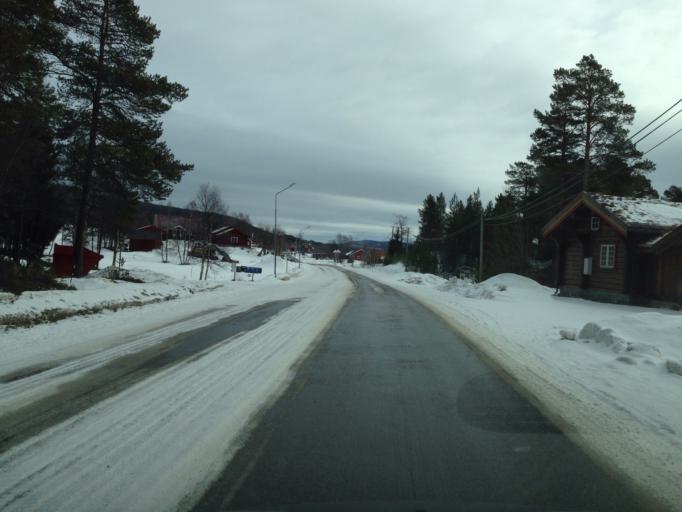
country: SE
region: Jaemtland
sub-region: Harjedalens Kommun
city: Sveg
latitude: 62.1129
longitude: 13.2640
